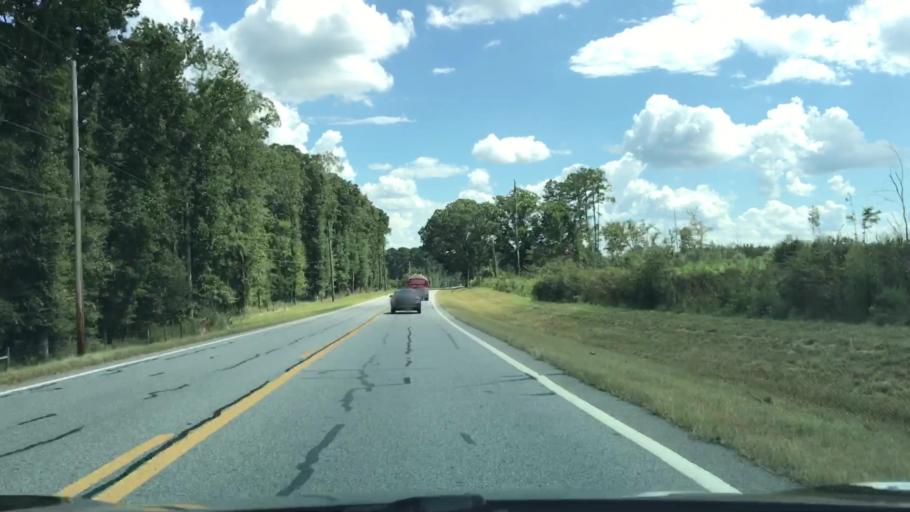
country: US
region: Georgia
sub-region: Oconee County
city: Watkinsville
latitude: 33.7886
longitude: -83.3192
